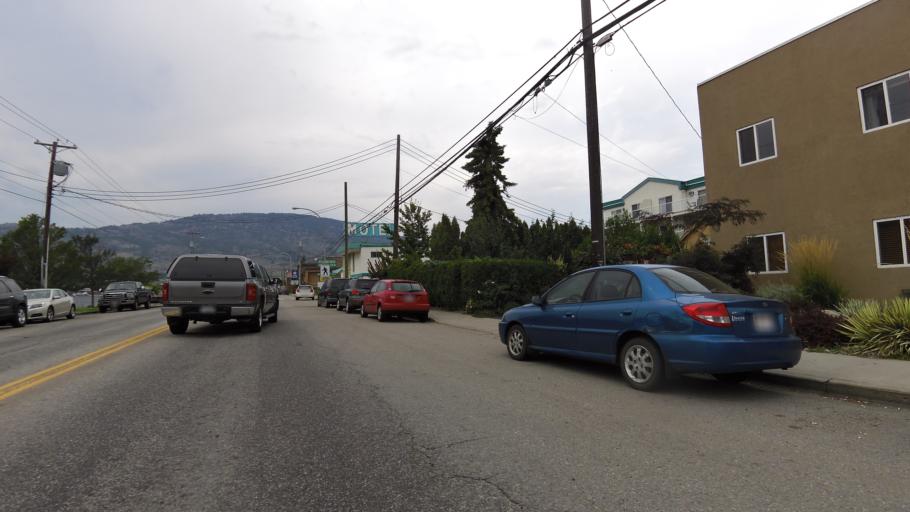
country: CA
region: British Columbia
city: Osoyoos
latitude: 49.0285
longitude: -119.4537
